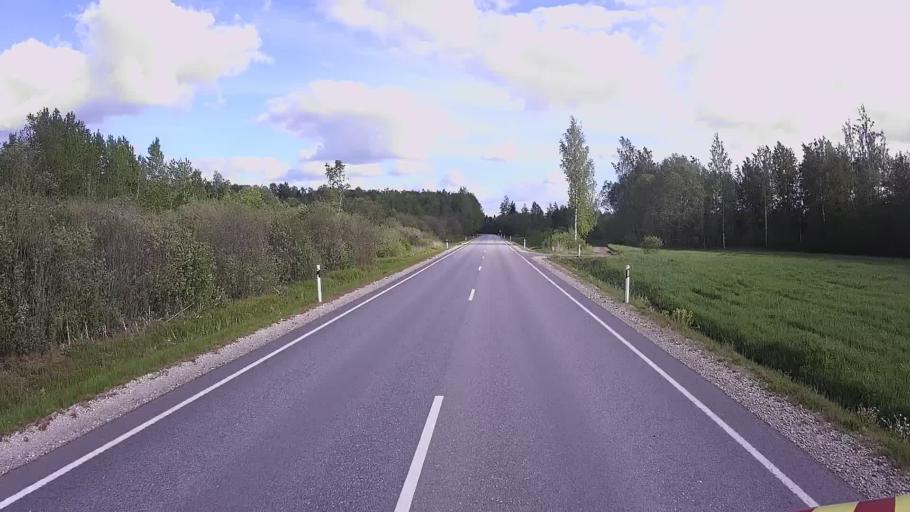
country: EE
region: Jogevamaa
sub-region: Mustvee linn
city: Mustvee
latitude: 58.8765
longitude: 26.8193
